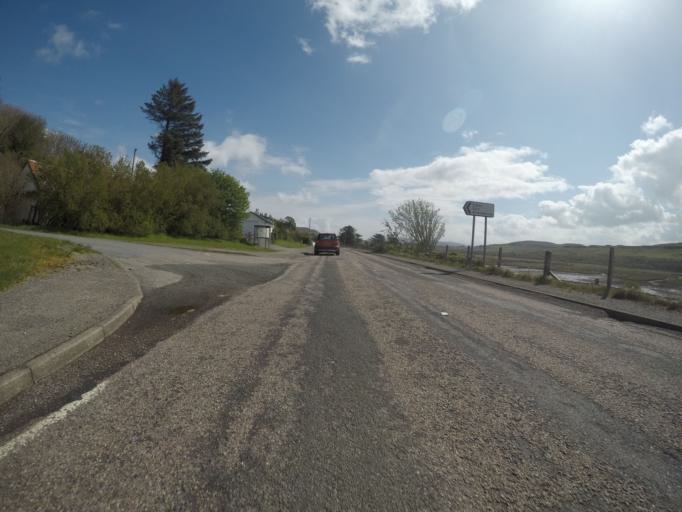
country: GB
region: Scotland
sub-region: Highland
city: Portree
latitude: 57.4850
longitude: -6.3076
